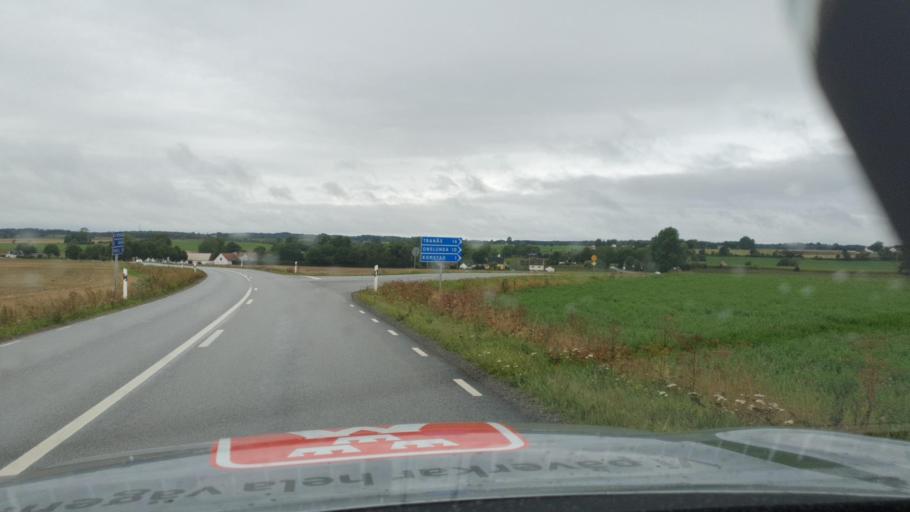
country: SE
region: Skane
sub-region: Simrishamns Kommun
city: Kivik
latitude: 55.5556
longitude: 14.1666
